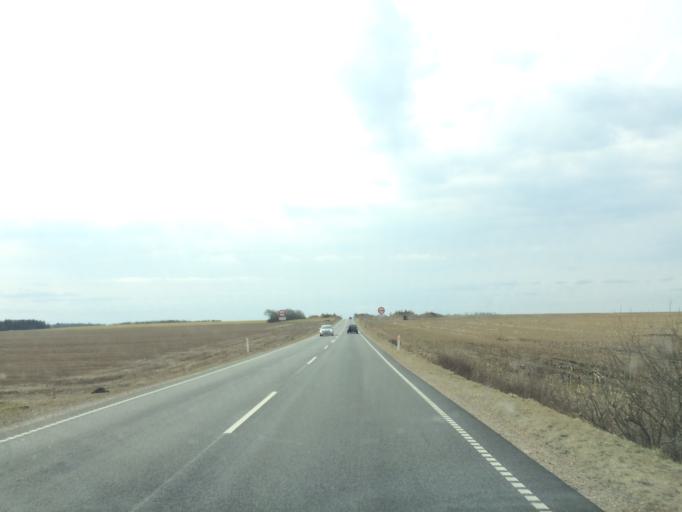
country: DK
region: Central Jutland
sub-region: Ringkobing-Skjern Kommune
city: Skjern
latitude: 56.0077
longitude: 8.5030
